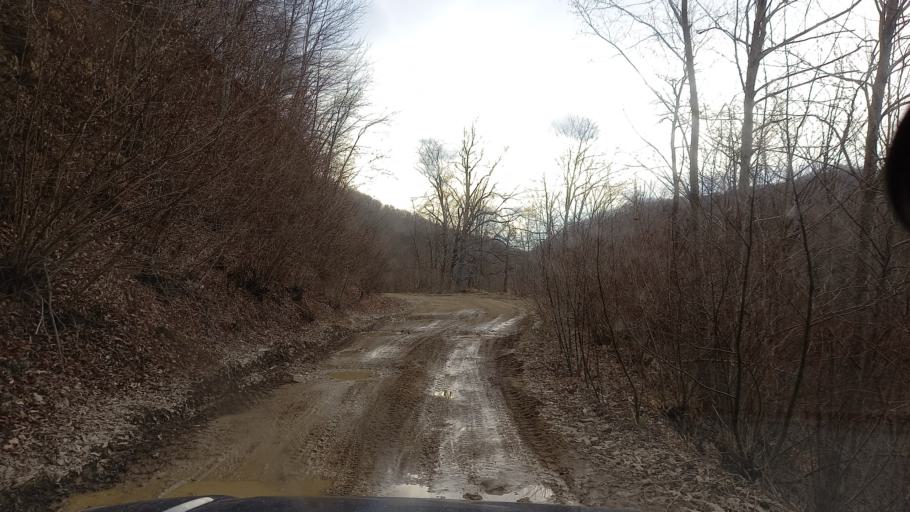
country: RU
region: Adygeya
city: Kamennomostskiy
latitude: 44.1683
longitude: 40.2990
